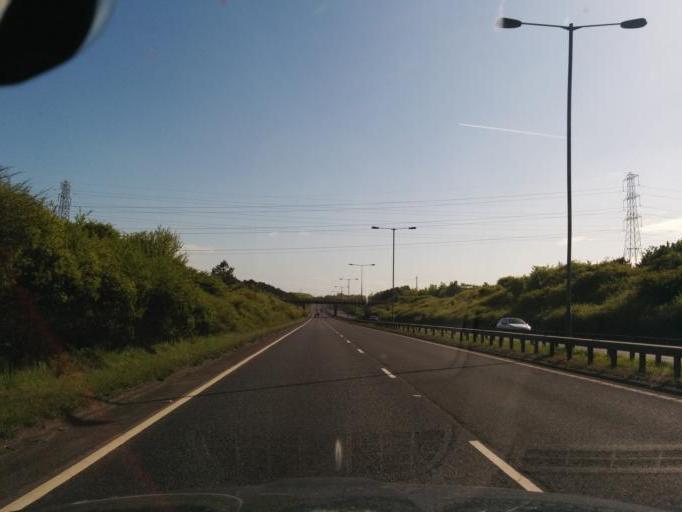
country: GB
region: England
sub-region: Northumberland
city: Ashington
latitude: 55.1493
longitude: -1.5489
